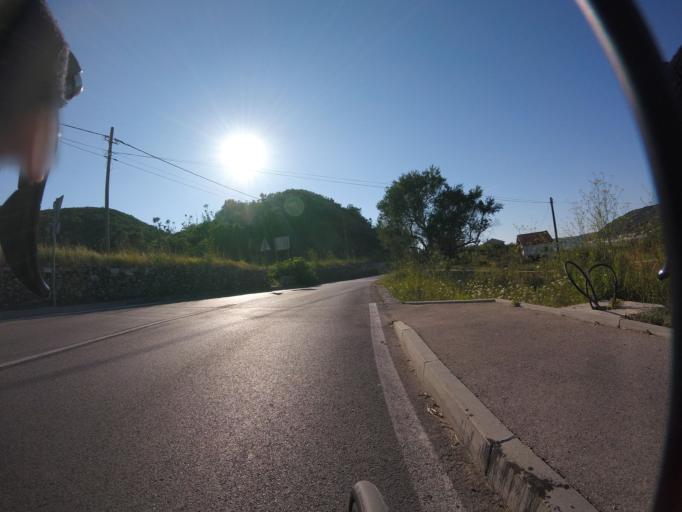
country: HR
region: Primorsko-Goranska
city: Supetarska Draga
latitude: 44.7941
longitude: 14.7301
